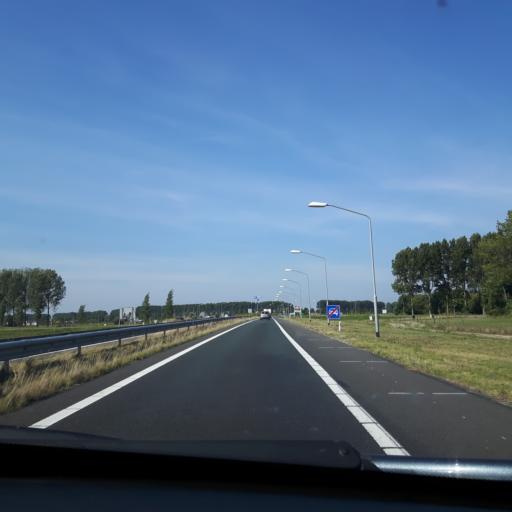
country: NL
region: Zeeland
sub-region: Gemeente Vlissingen
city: Vlissingen
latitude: 51.3473
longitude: 3.5465
